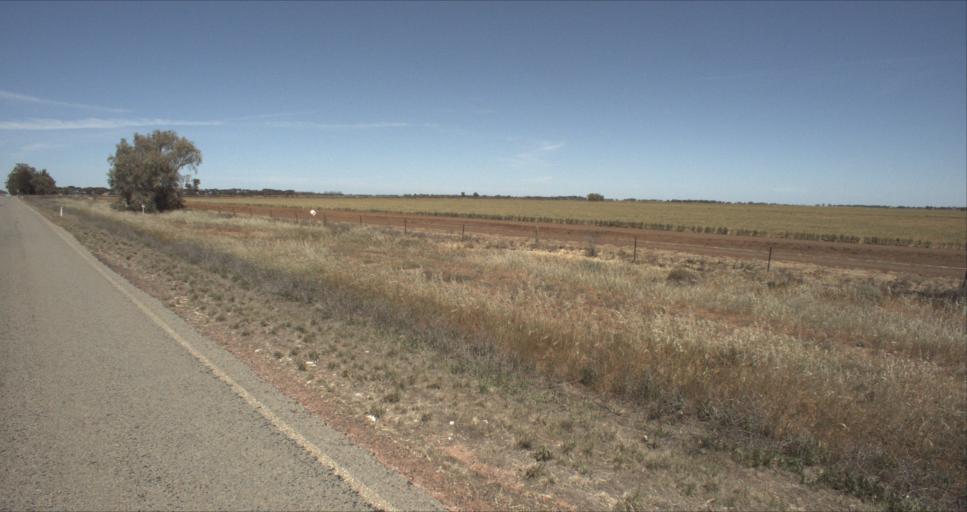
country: AU
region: New South Wales
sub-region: Leeton
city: Leeton
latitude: -34.4620
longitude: 146.2940
